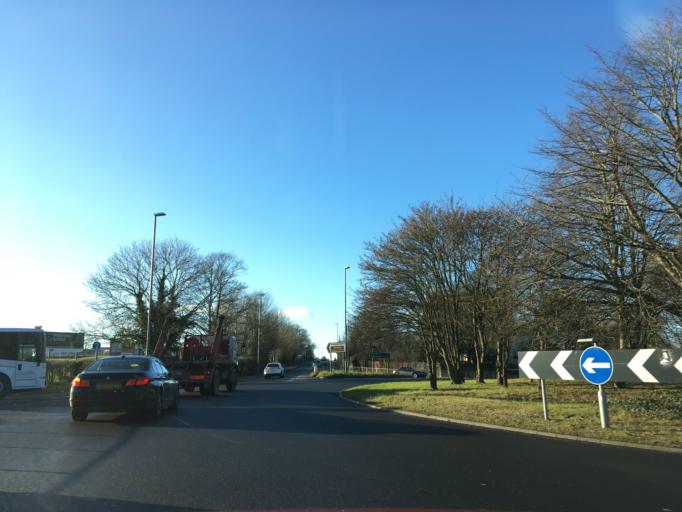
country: GB
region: England
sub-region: Bath and North East Somerset
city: Keynsham
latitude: 51.4123
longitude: -2.4821
